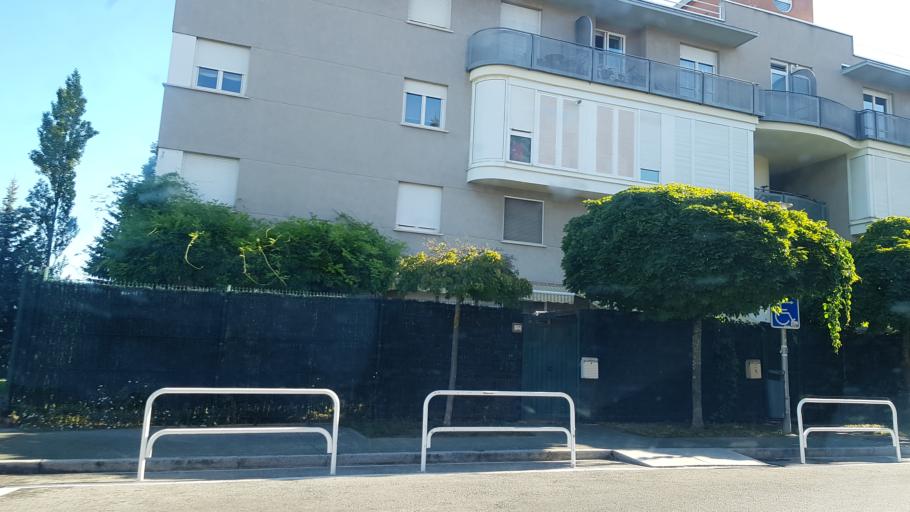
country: ES
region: Navarre
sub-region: Provincia de Navarra
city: Burlata
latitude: 42.8140
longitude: -1.6137
